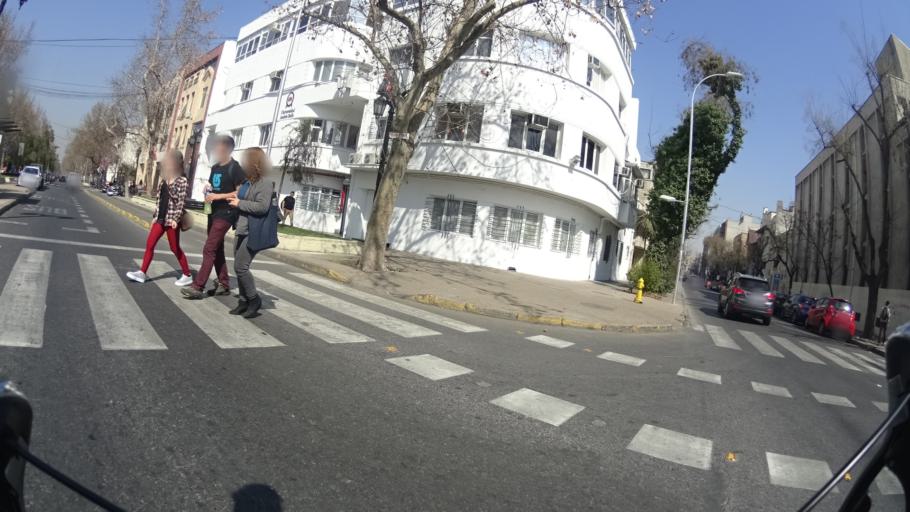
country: CL
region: Santiago Metropolitan
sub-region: Provincia de Santiago
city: Santiago
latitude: -33.4511
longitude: -70.6677
